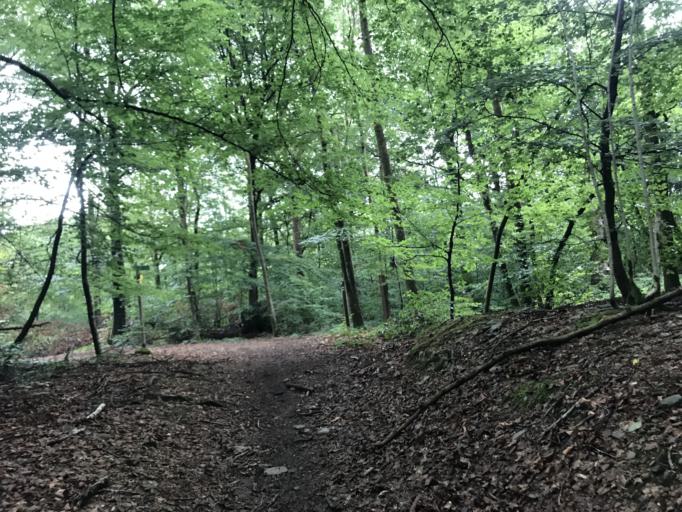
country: FR
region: Champagne-Ardenne
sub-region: Departement des Ardennes
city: Thilay
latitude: 49.8950
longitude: 4.7817
